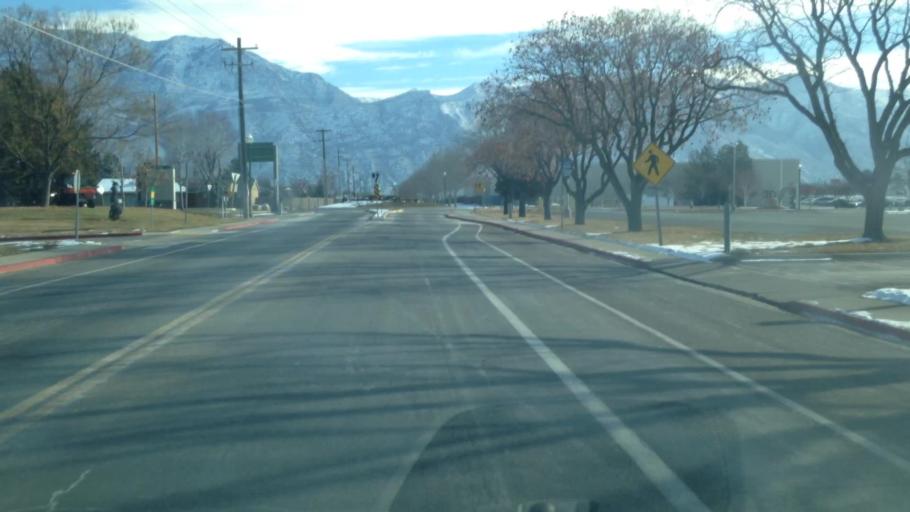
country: US
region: Utah
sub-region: Utah County
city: Orem
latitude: 40.2753
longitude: -111.7062
